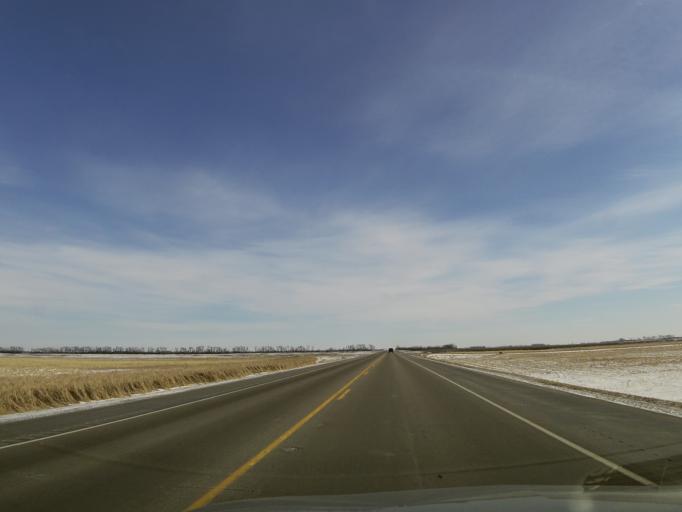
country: US
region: North Dakota
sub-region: Walsh County
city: Grafton
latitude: 48.4126
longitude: -97.3672
